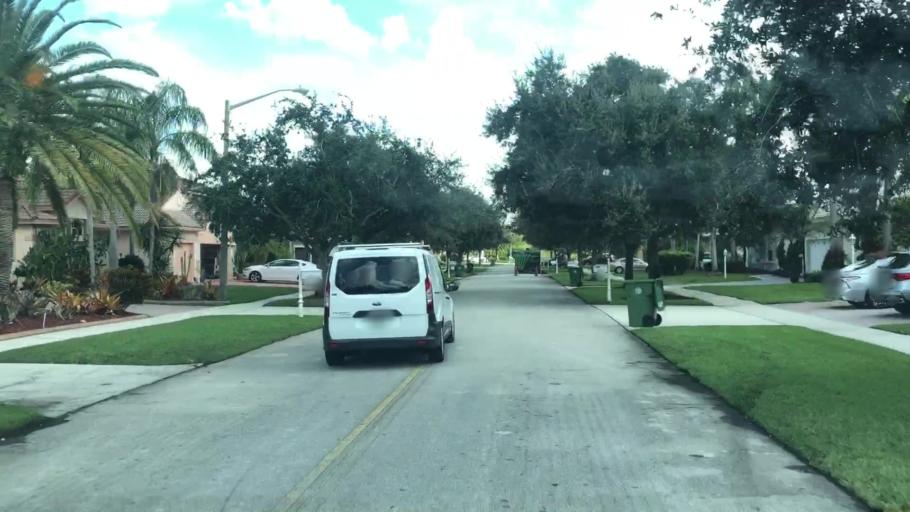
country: US
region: Florida
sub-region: Broward County
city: Southwest Ranches
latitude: 26.0329
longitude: -80.3685
